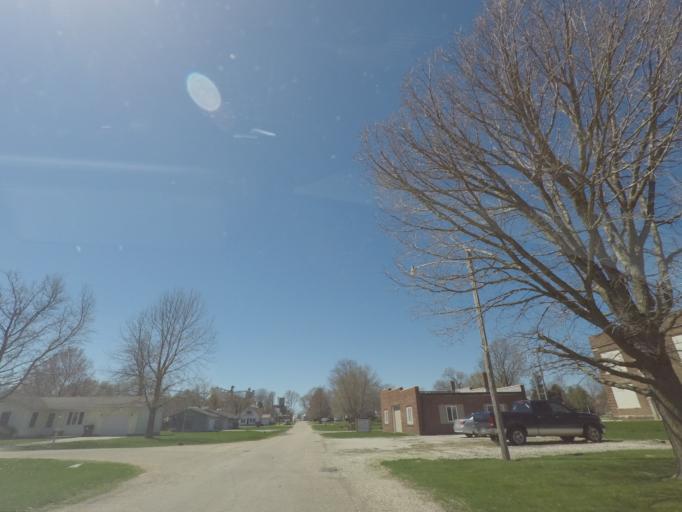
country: US
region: Illinois
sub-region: Macon County
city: Warrensburg
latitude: 39.9665
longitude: -89.1573
